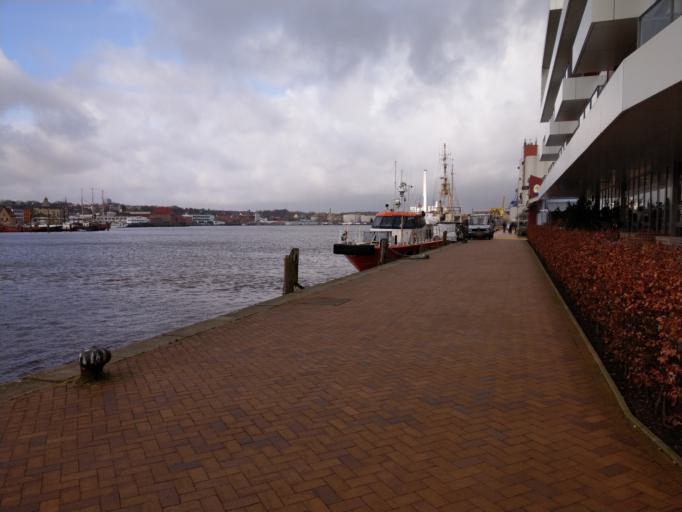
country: DE
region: Schleswig-Holstein
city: Flensburg
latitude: 54.7930
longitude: 9.4378
